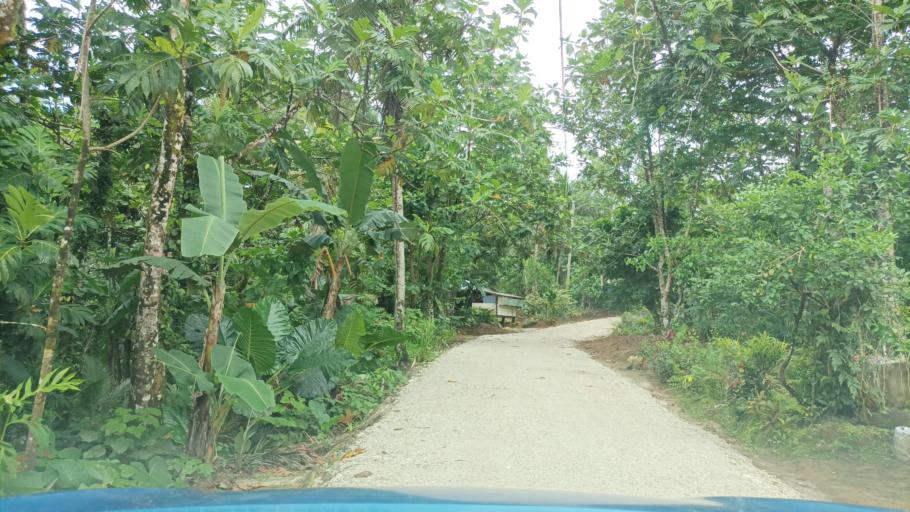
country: FM
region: Pohnpei
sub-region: Sokehs Municipality
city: Palikir - National Government Center
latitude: 6.8563
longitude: 158.1597
